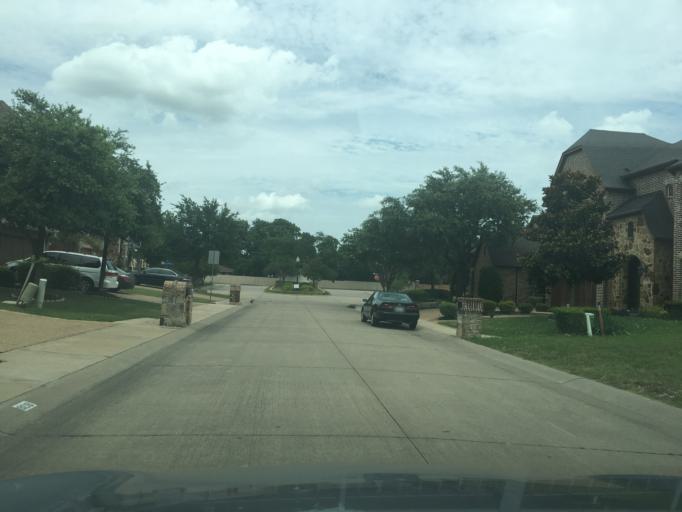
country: US
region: Texas
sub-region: Dallas County
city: Richardson
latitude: 32.9372
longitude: -96.7277
